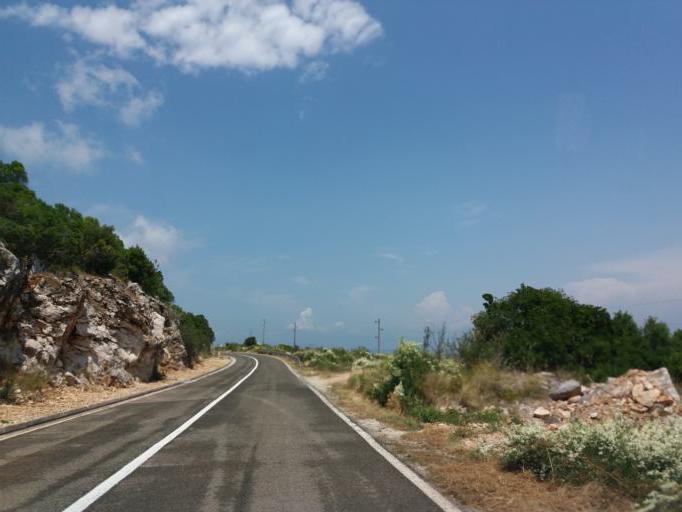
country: HR
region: Zadarska
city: Sali
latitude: 44.0010
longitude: 15.0558
